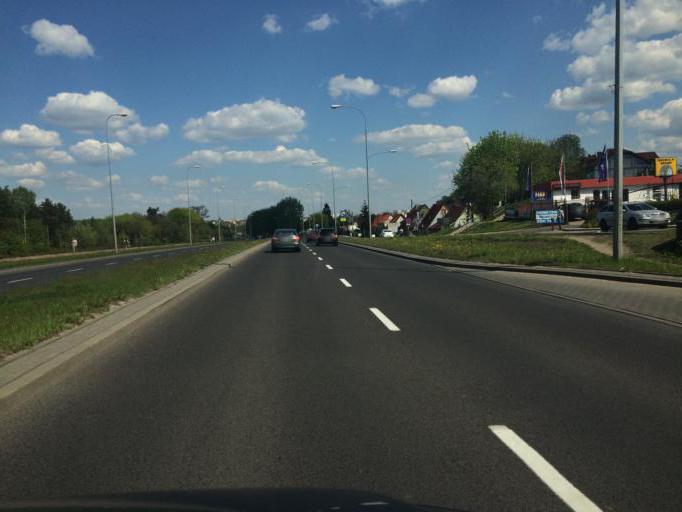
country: PL
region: Warmian-Masurian Voivodeship
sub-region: Olsztyn
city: Kortowo
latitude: 53.7696
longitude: 20.4354
